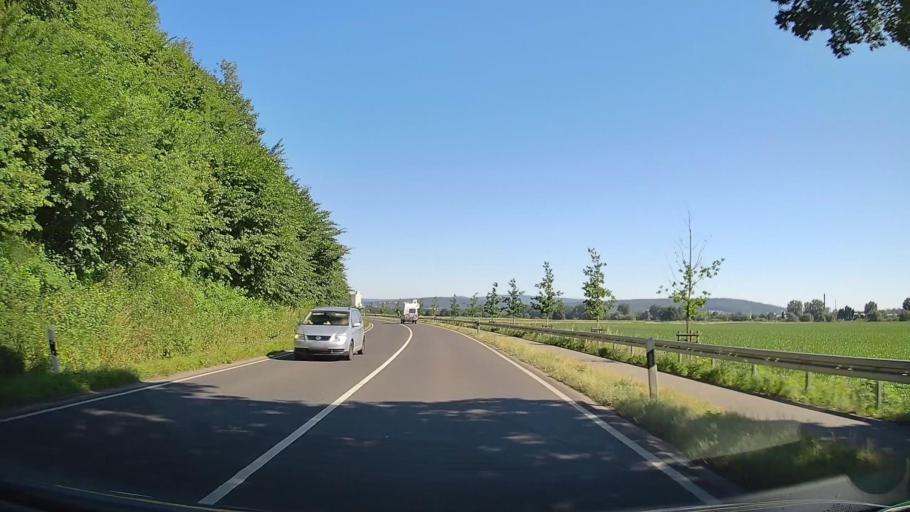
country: DE
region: Lower Saxony
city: Hameln
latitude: 52.0788
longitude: 9.3611
